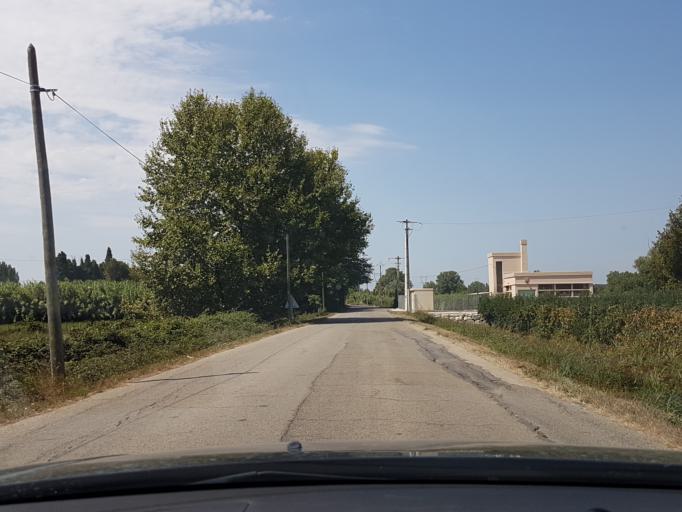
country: FR
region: Provence-Alpes-Cote d'Azur
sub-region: Departement des Bouches-du-Rhone
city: Molleges
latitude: 43.8045
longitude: 4.8991
